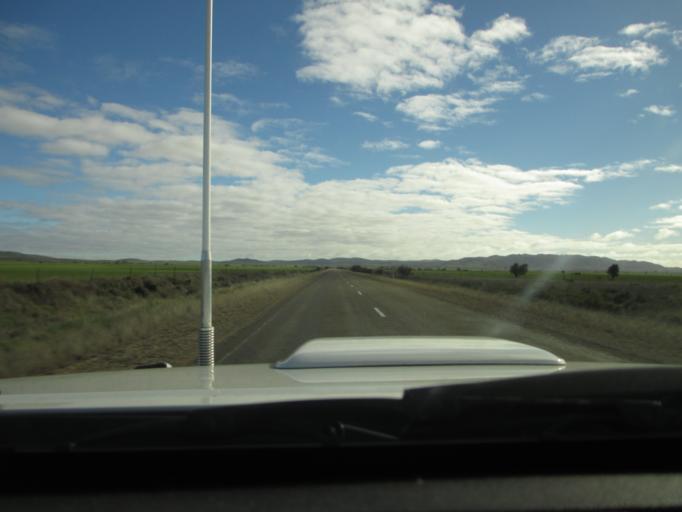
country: AU
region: South Australia
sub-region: Peterborough
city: Peterborough
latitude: -32.6615
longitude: 138.6055
